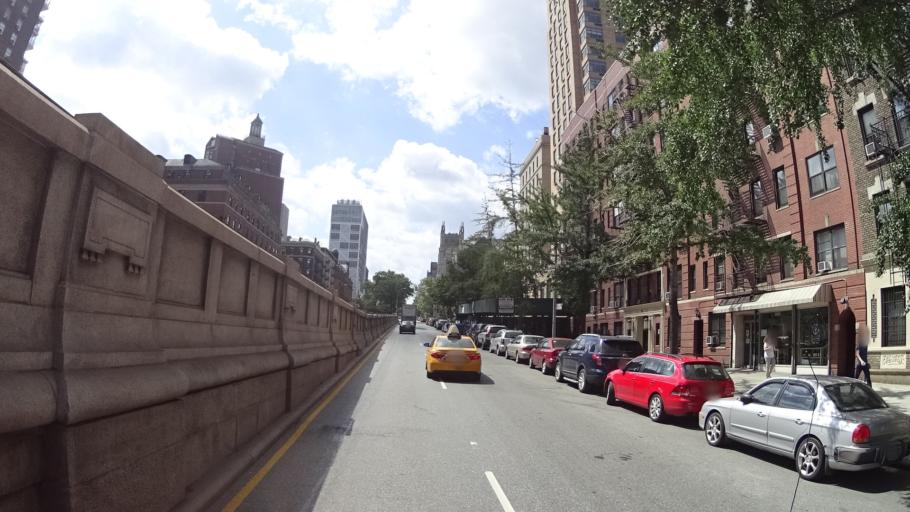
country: US
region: New Jersey
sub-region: Bergen County
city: Edgewater
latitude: 40.8131
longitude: -73.9603
